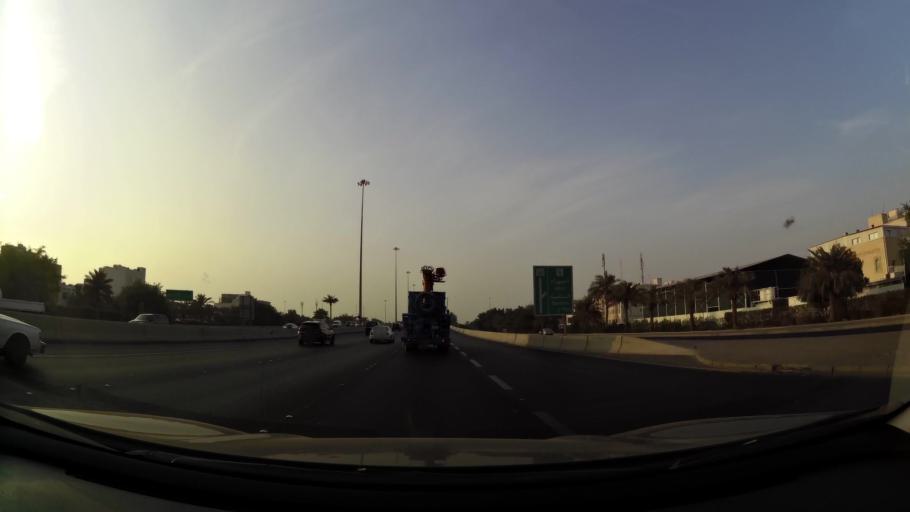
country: KW
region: Muhafazat Hawalli
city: Ar Rumaythiyah
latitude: 29.3009
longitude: 48.0637
